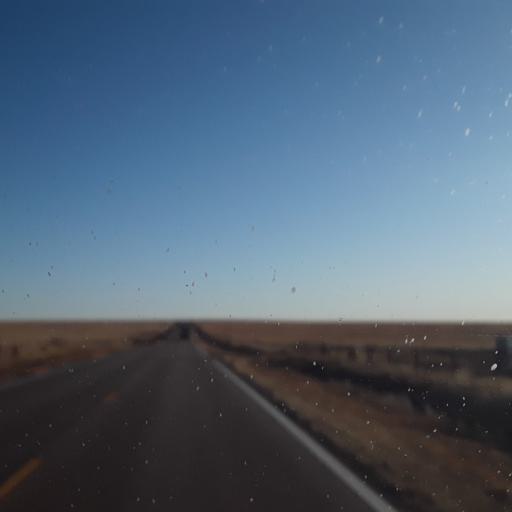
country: US
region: Kansas
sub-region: Wallace County
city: Sharon Springs
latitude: 39.0327
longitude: -101.7386
